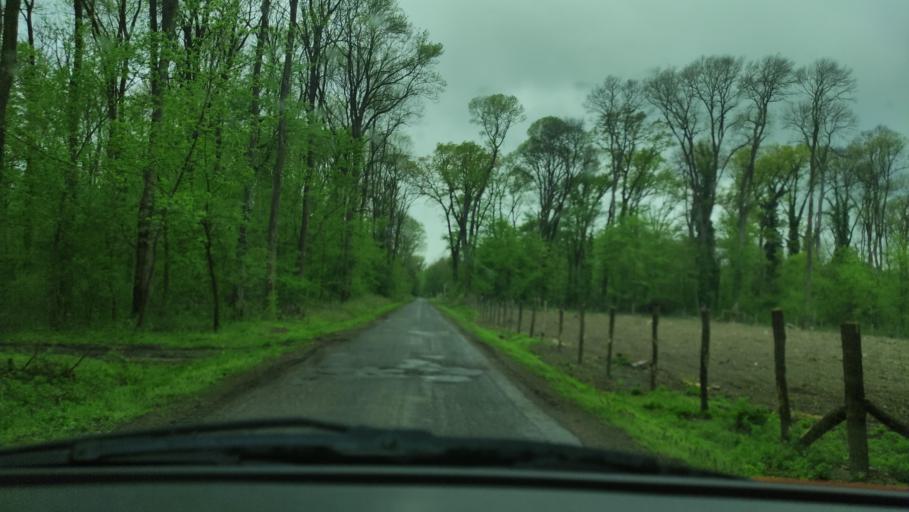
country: HU
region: Baranya
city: Mohacs
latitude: 45.9102
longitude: 18.7364
